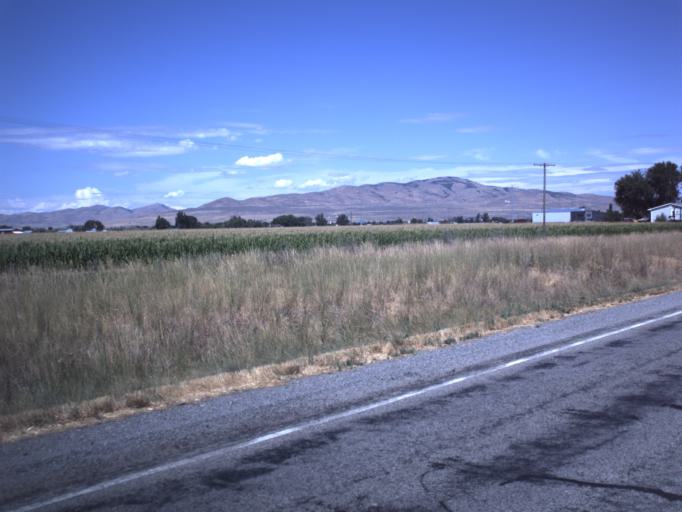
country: US
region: Utah
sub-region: Box Elder County
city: Elwood
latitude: 41.6744
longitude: -112.1410
